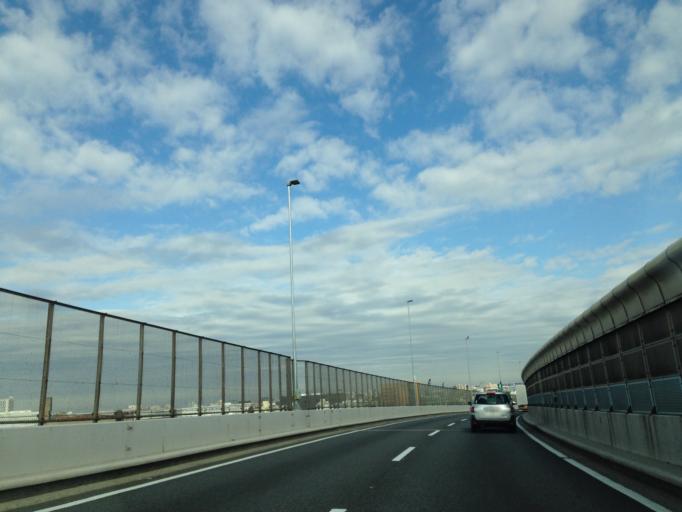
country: JP
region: Saitama
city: Kawaguchi
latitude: 35.7810
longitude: 139.7455
